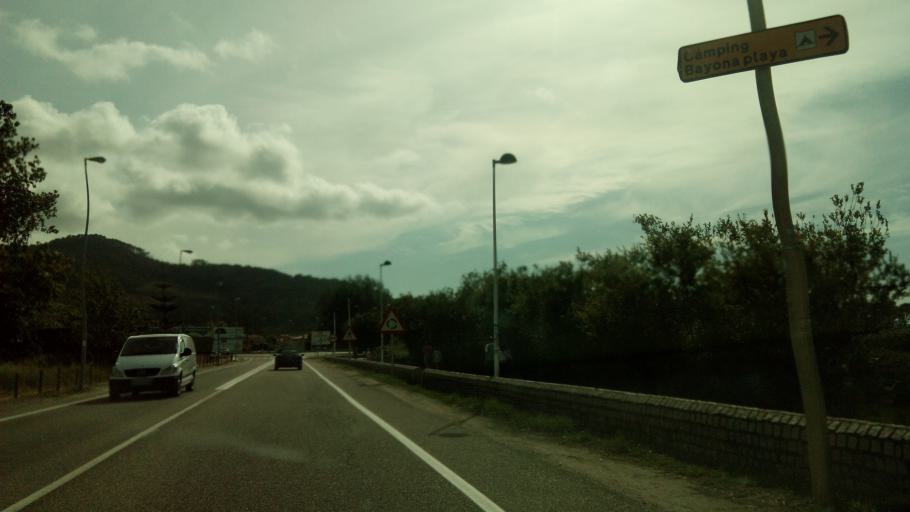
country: ES
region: Galicia
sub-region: Provincia de Pontevedra
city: Baiona
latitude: 42.1130
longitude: -8.8199
